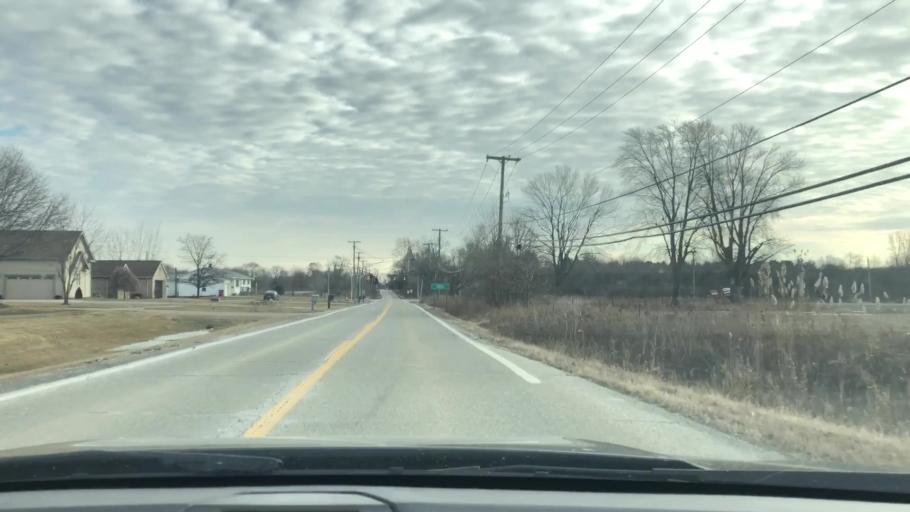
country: US
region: Michigan
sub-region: Macomb County
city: Shelby
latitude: 42.7285
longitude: -83.0195
